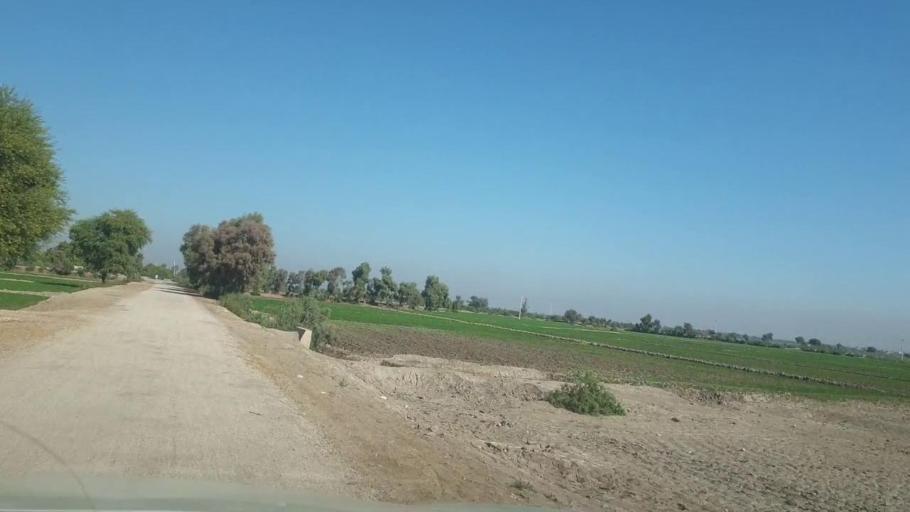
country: PK
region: Sindh
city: Bhan
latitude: 26.5266
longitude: 67.6436
